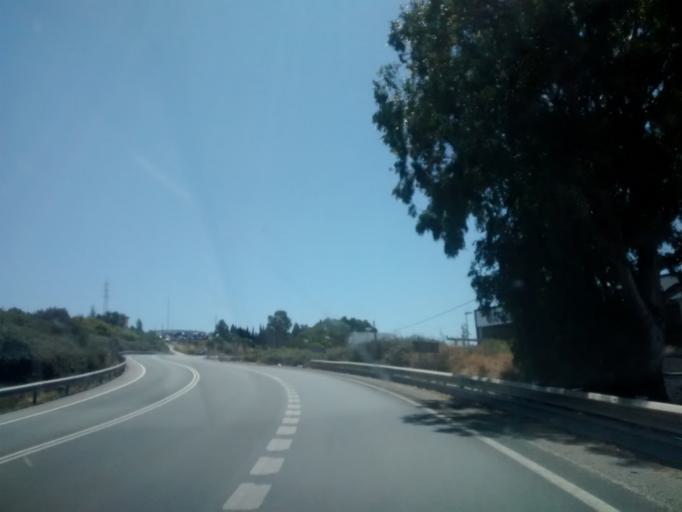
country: ES
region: Andalusia
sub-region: Provincia de Cadiz
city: Algeciras
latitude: 36.0997
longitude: -5.4668
